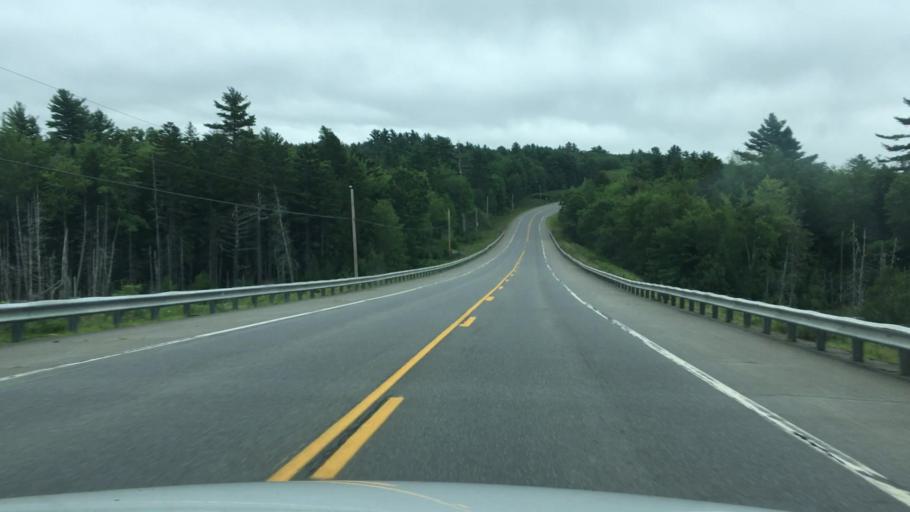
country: US
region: Maine
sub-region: Hancock County
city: Franklin
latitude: 44.8399
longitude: -68.1563
